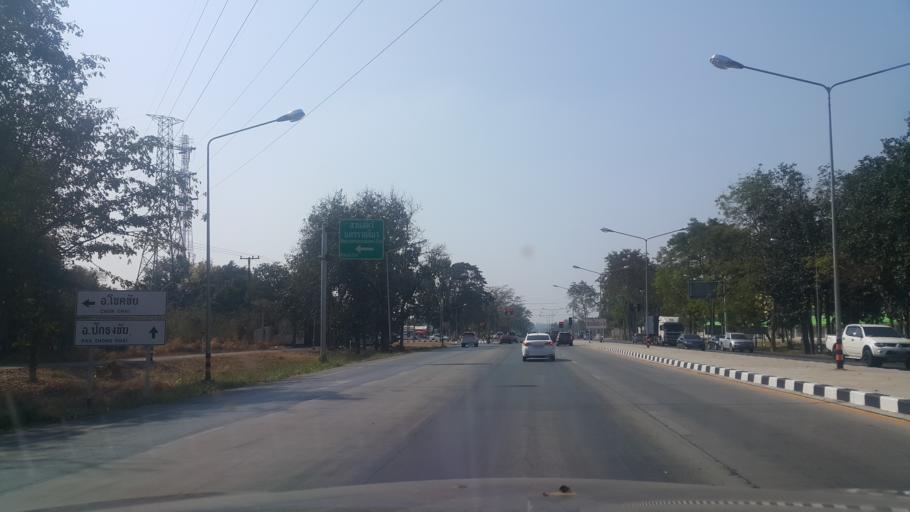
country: TH
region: Nakhon Ratchasima
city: Nakhon Ratchasima
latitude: 14.8556
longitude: 102.0678
